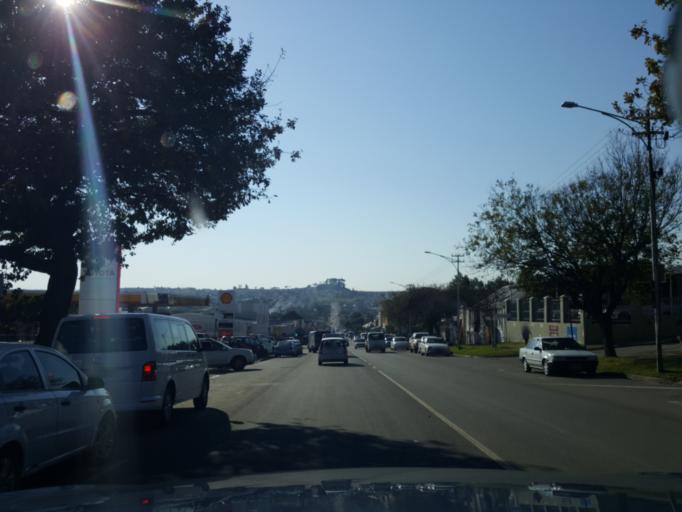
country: ZA
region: Eastern Cape
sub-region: Cacadu District Municipality
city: Grahamstown
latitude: -33.3131
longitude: 26.5293
